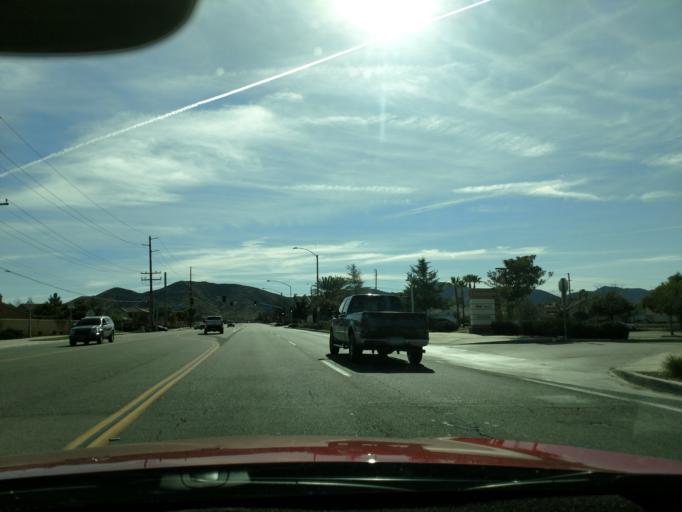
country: US
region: California
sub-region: Riverside County
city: Hemet
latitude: 33.7266
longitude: -117.0067
